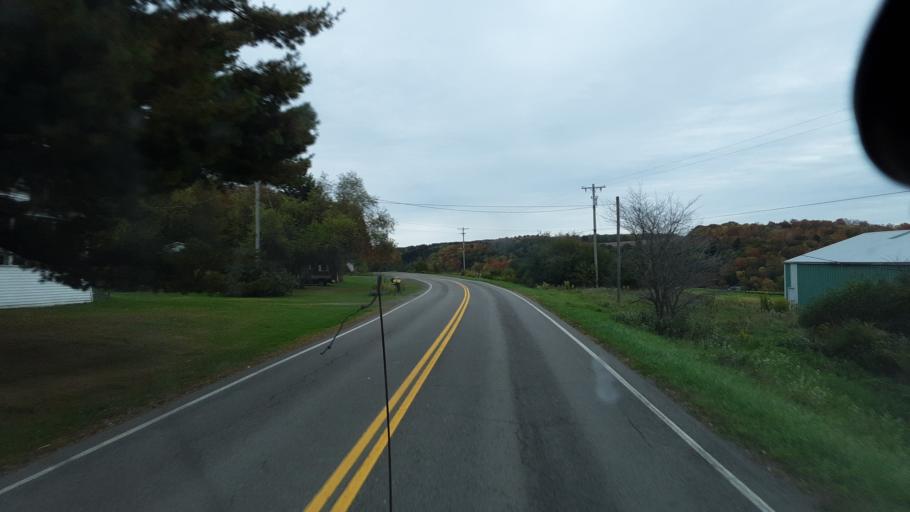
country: US
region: New York
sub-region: Allegany County
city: Andover
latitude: 42.0848
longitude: -77.7979
